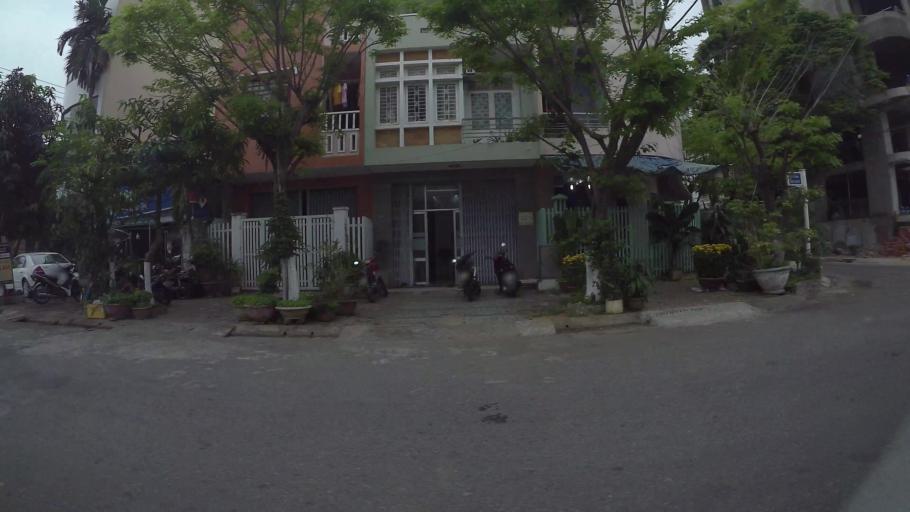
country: VN
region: Da Nang
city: Cam Le
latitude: 16.0314
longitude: 108.2148
